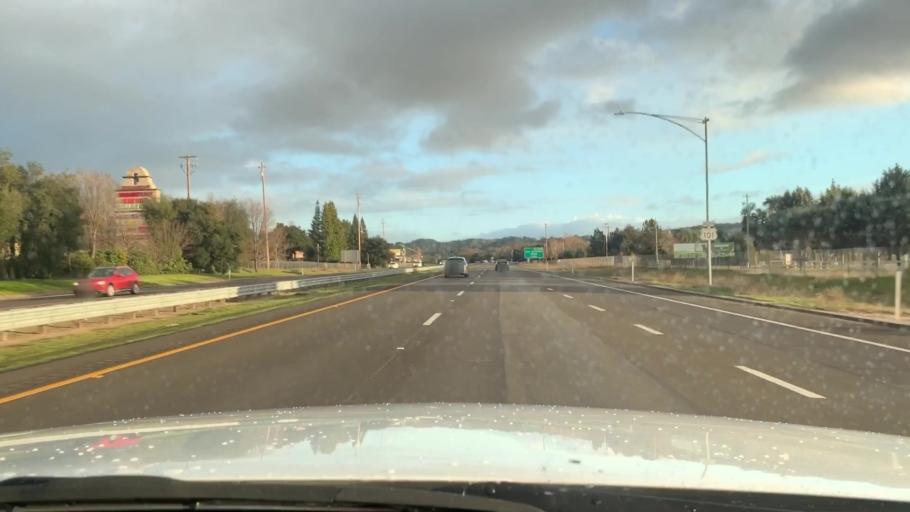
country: US
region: California
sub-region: San Luis Obispo County
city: Atascadero
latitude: 35.5109
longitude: -120.6990
